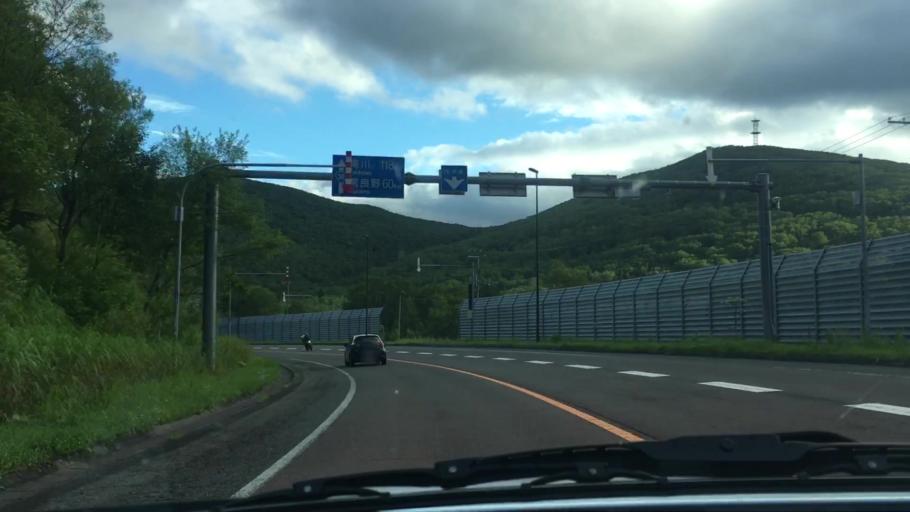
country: JP
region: Hokkaido
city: Shimo-furano
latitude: 43.1333
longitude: 142.7622
